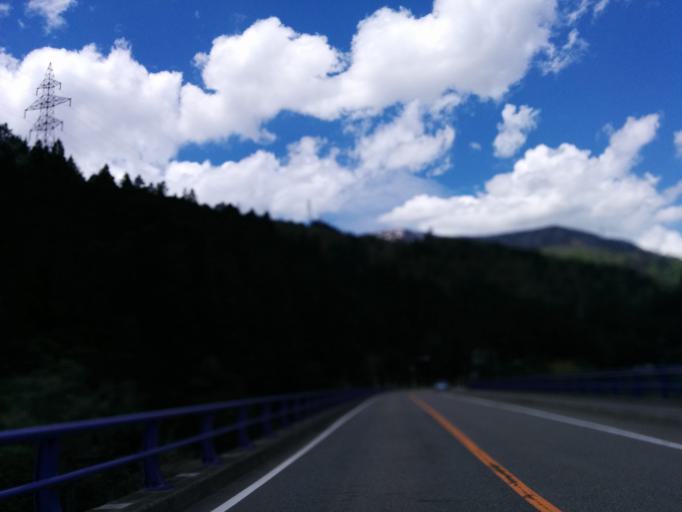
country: JP
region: Toyama
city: Fukumitsu
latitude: 36.3702
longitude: 136.8691
